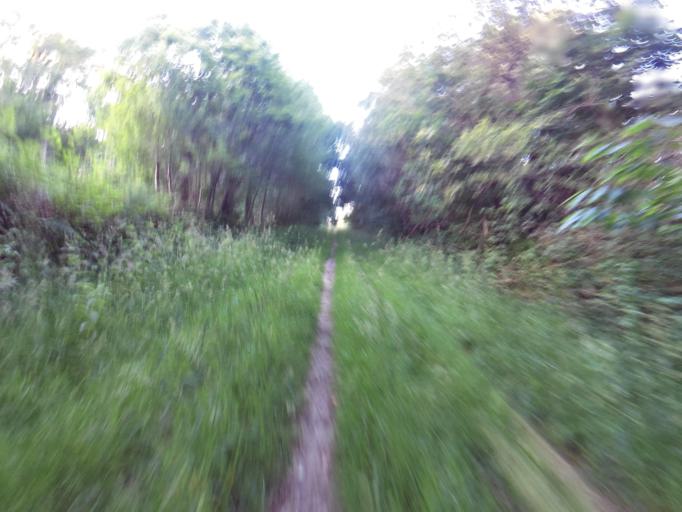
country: FR
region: Brittany
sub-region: Departement du Morbihan
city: Molac
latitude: 47.7534
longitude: -2.4122
